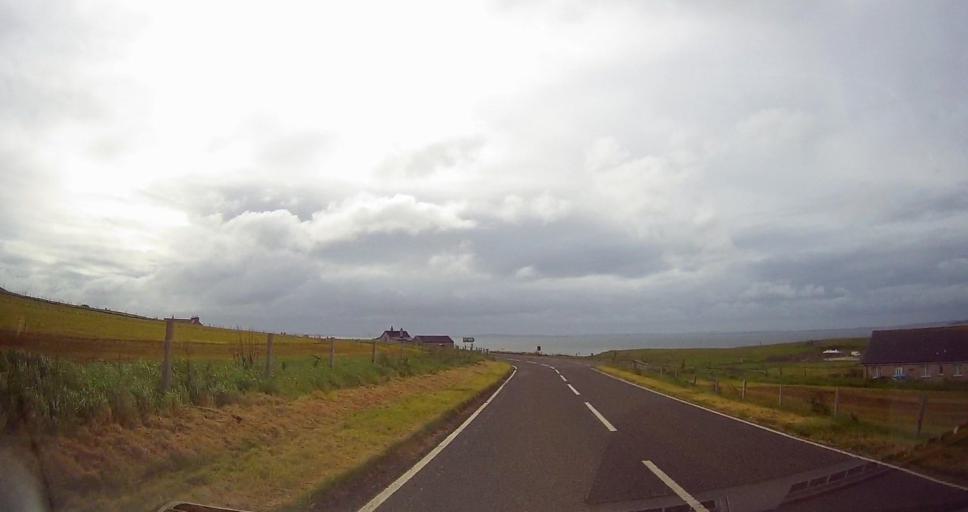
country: GB
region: Scotland
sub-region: Orkney Islands
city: Stromness
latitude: 58.9200
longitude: -3.1829
